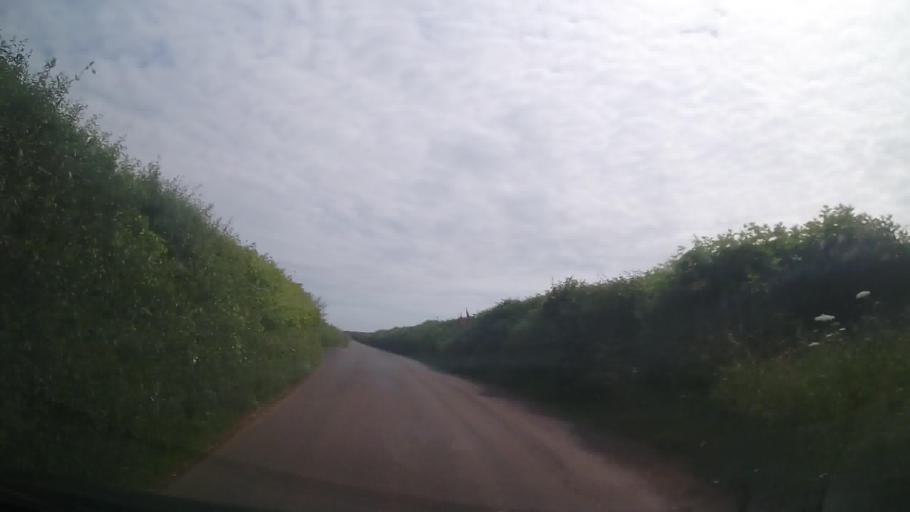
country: GB
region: England
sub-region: Devon
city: Salcombe
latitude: 50.2486
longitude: -3.6824
